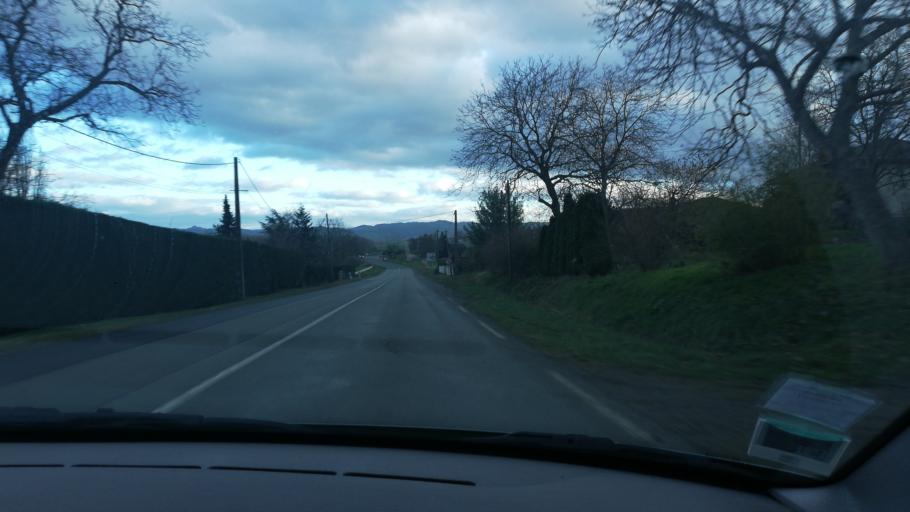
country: FR
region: Auvergne
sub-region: Departement du Puy-de-Dome
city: Vertaizon
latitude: 45.7653
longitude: 3.3040
